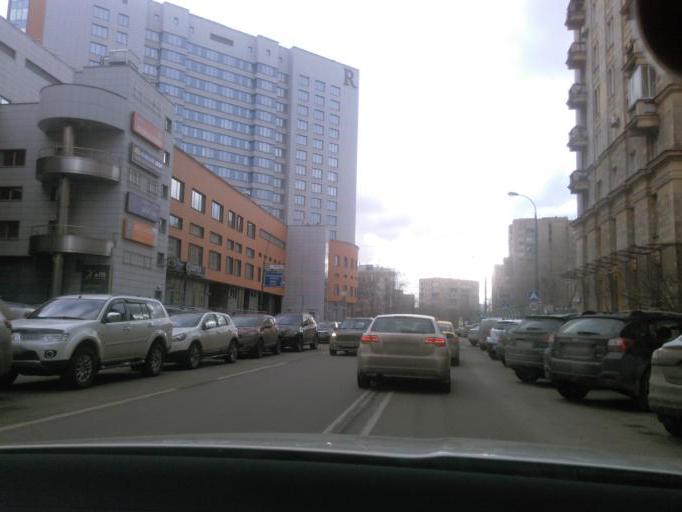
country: RU
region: Moskovskaya
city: Dorogomilovo
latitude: 55.7835
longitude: 37.5589
